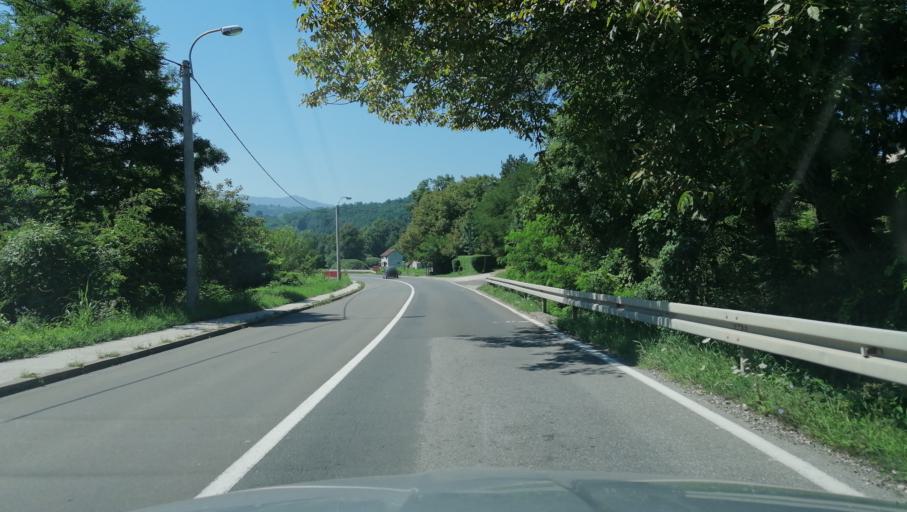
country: RS
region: Central Serbia
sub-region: Raski Okrug
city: Kraljevo
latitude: 43.6943
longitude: 20.5836
